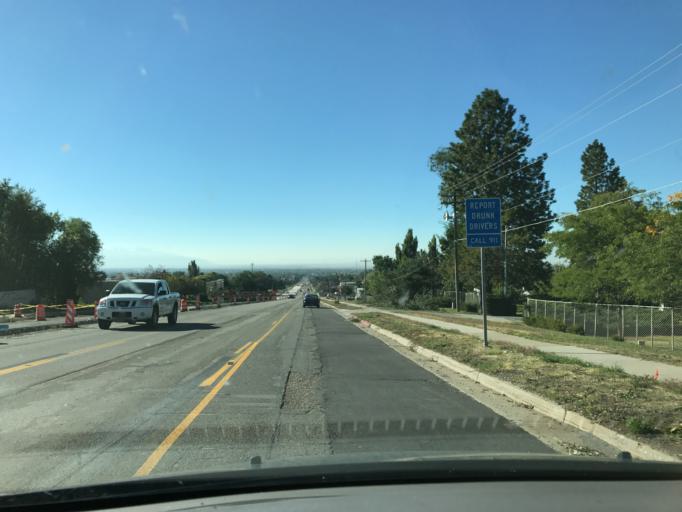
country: US
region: Utah
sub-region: Davis County
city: Hill Air Force Bace
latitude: 41.1007
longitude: -111.9735
